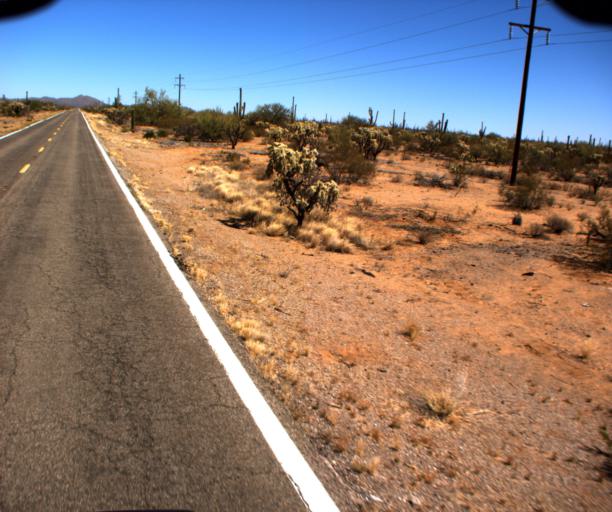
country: US
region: Arizona
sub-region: Pima County
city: Sells
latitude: 32.1070
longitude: -112.0710
